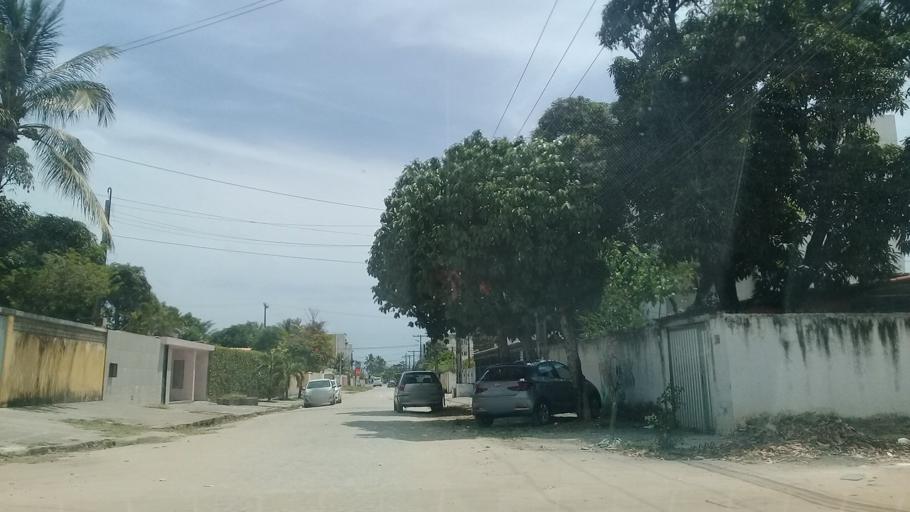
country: BR
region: Pernambuco
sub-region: Paulista
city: Paulista
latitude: -7.9445
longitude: -34.8281
